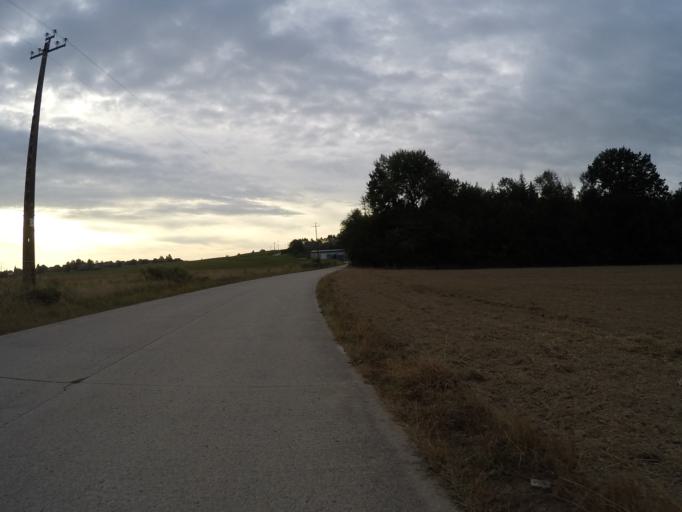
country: BE
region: Wallonia
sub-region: Province de Namur
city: Assesse
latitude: 50.3420
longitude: 5.0408
